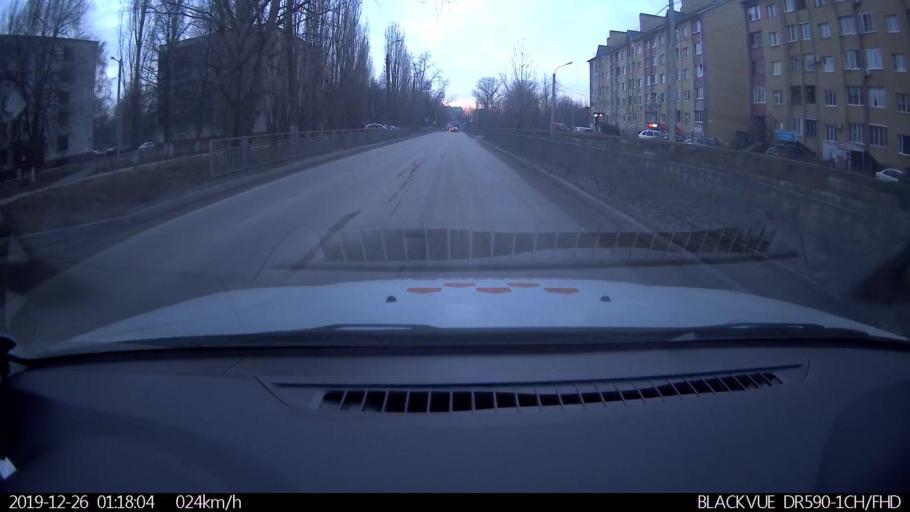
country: RU
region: Nizjnij Novgorod
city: Nizhniy Novgorod
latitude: 56.2708
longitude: 43.8944
